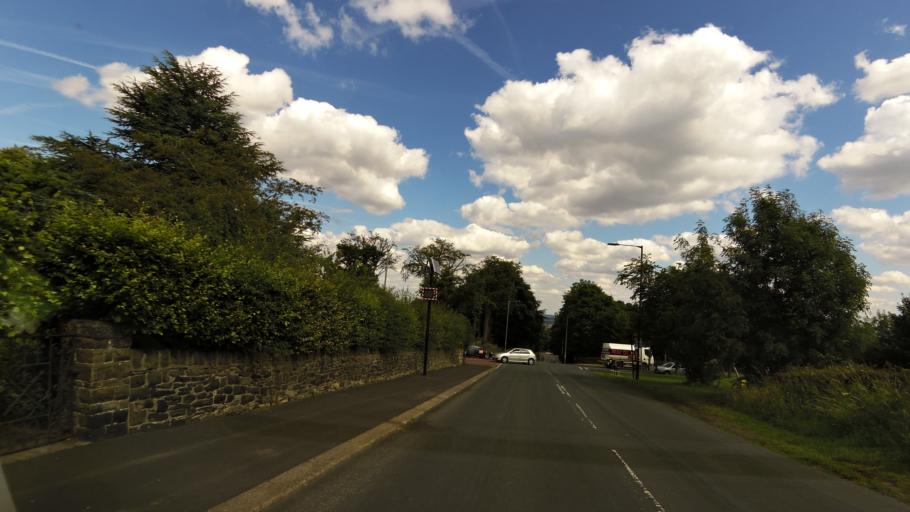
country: GB
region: England
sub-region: Sheffield
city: Oughtibridge
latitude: 53.4368
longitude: -1.5000
